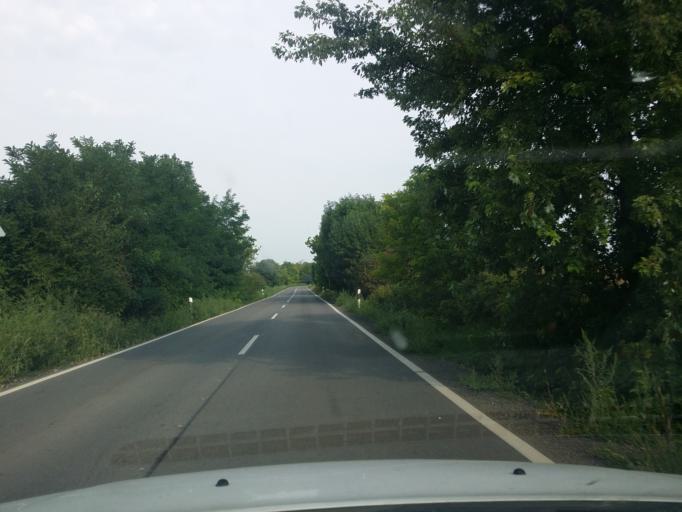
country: HU
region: Pest
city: Acsa
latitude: 47.7503
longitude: 19.3700
